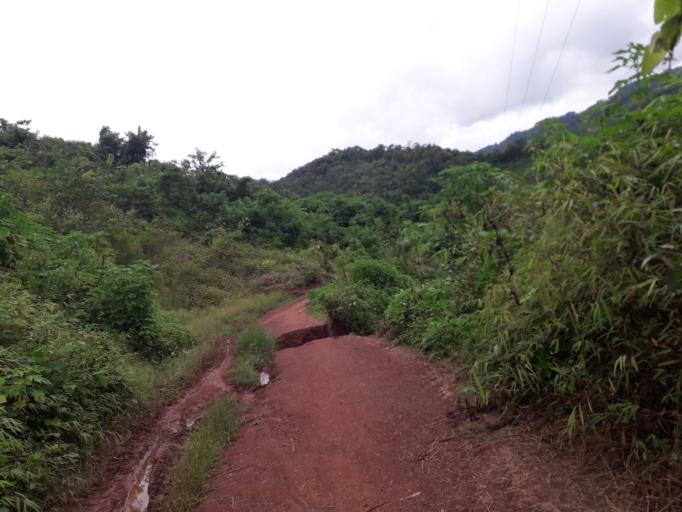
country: CN
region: Yunnan
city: Menglie
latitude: 22.2122
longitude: 101.6597
